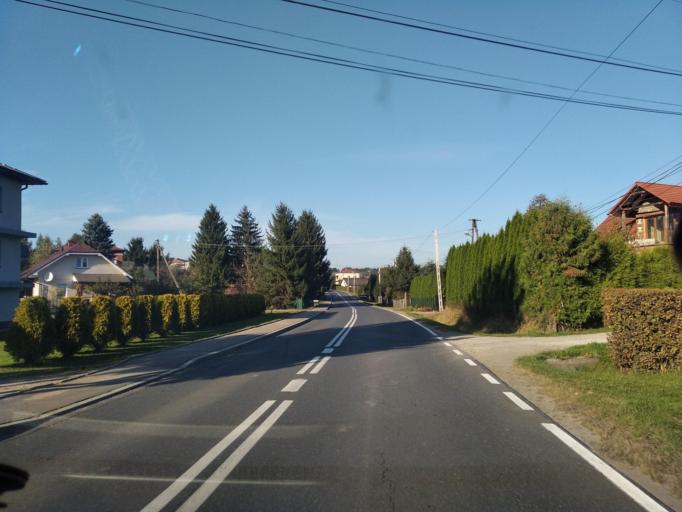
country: PL
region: Subcarpathian Voivodeship
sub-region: Powiat brzozowski
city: Humniska
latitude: 49.6791
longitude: 22.0338
